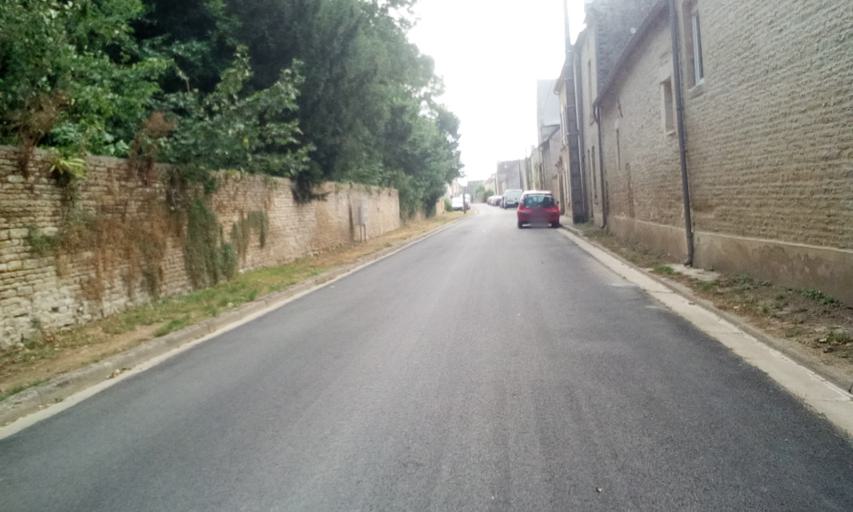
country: FR
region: Lower Normandy
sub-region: Departement du Calvados
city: Courseulles-sur-Mer
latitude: 49.3104
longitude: -0.4909
